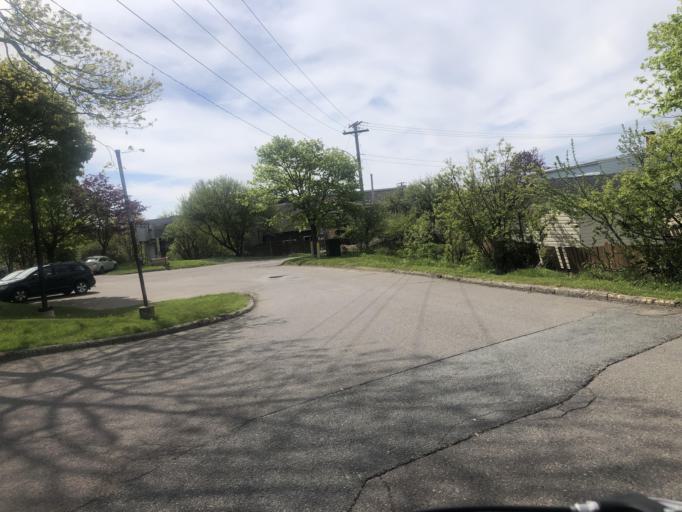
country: CA
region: New Brunswick
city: Saint John
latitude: 45.2818
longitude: -66.0809
